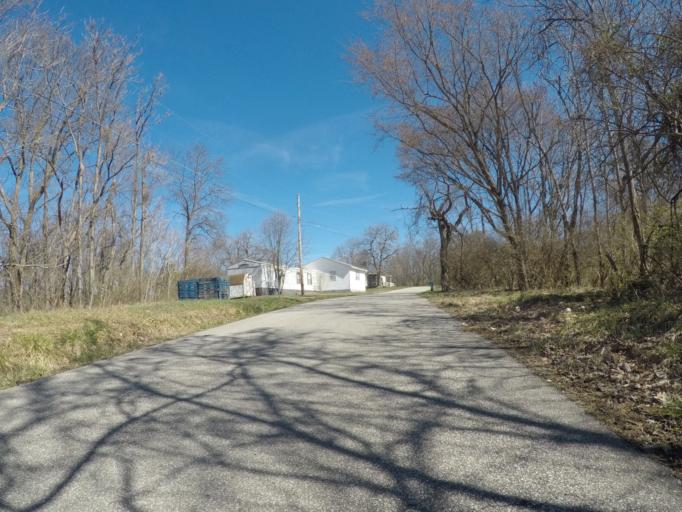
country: US
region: West Virginia
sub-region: Cabell County
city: Huntington
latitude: 38.4603
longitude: -82.4957
